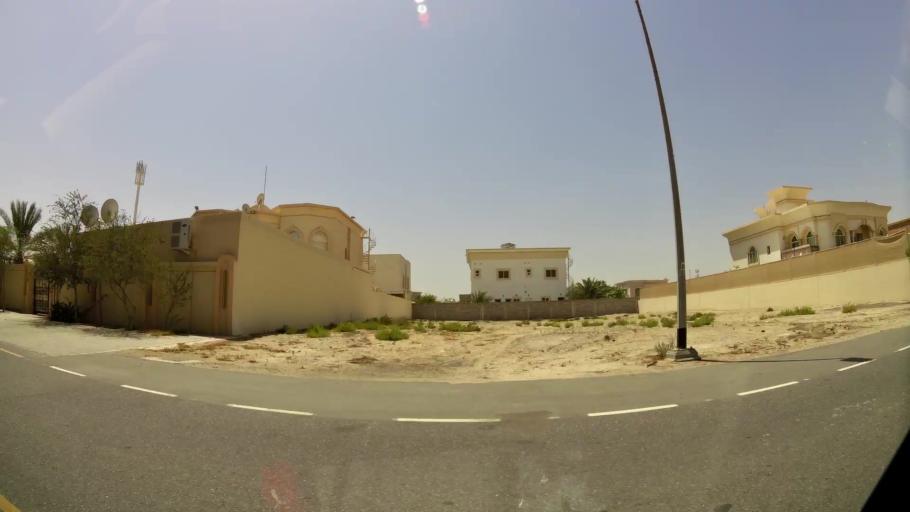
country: AE
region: Dubai
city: Dubai
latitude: 25.1037
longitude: 55.2218
